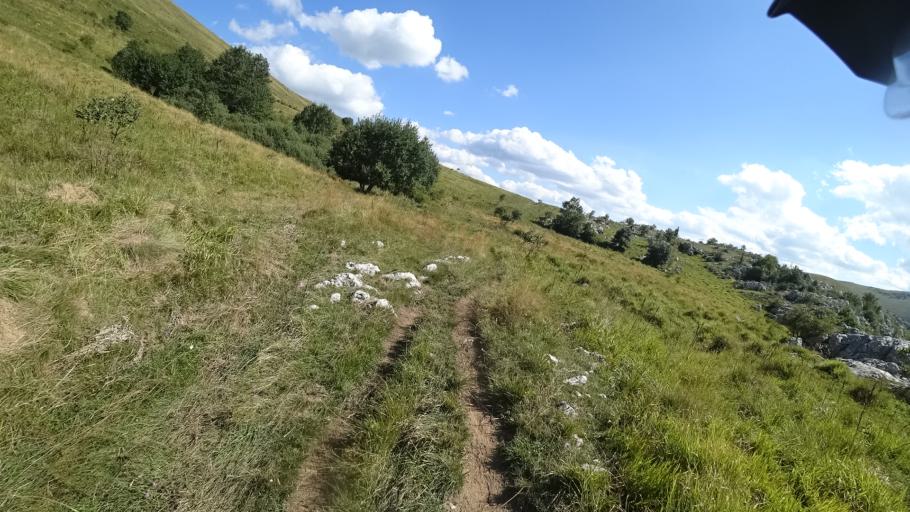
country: HR
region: Zadarska
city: Gracac
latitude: 44.4042
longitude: 16.0065
